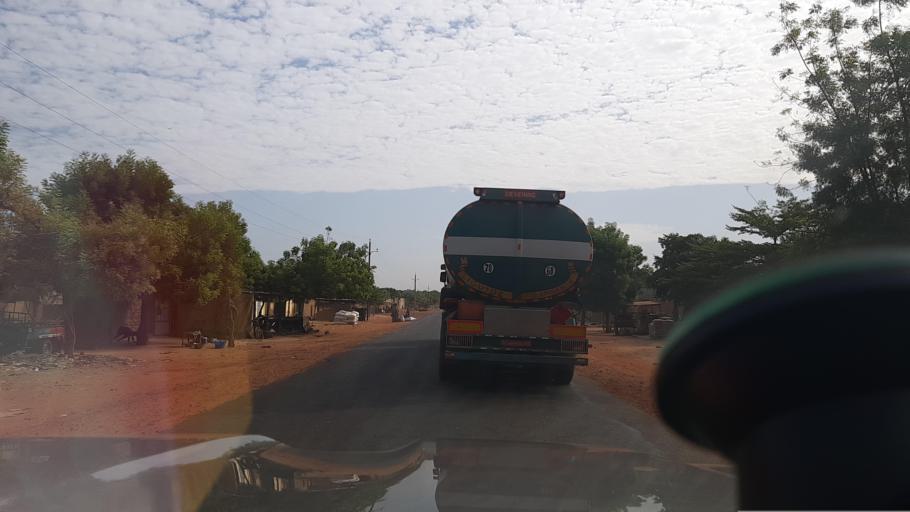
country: ML
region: Segou
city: Segou
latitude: 13.4954
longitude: -6.1701
